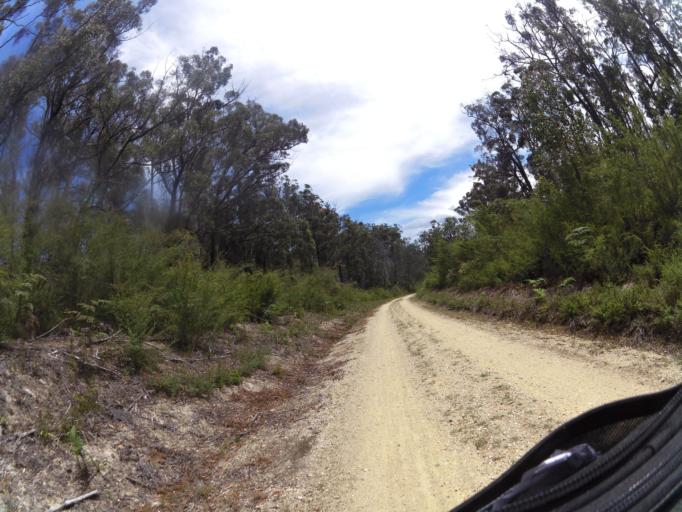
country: AU
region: Victoria
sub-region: East Gippsland
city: Lakes Entrance
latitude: -37.7451
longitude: 148.0342
